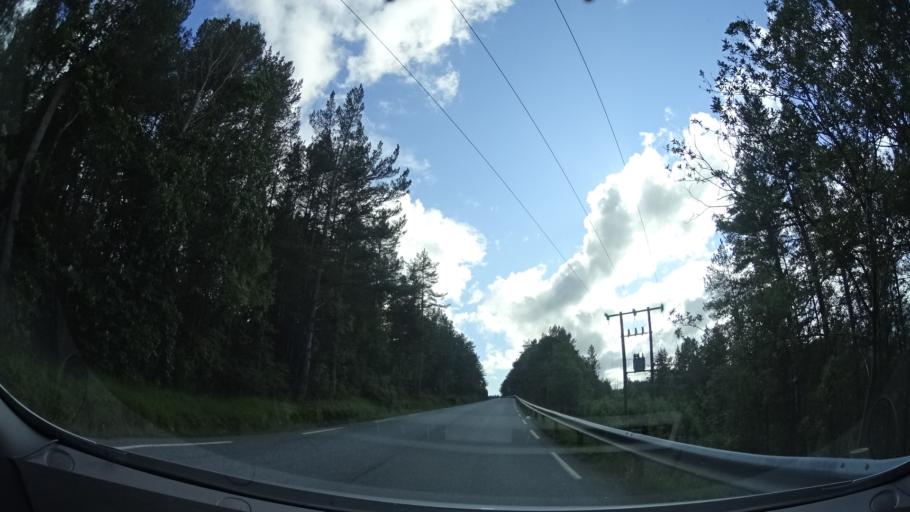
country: NO
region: More og Romsdal
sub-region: Halsa
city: Liaboen
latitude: 63.1314
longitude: 8.3862
